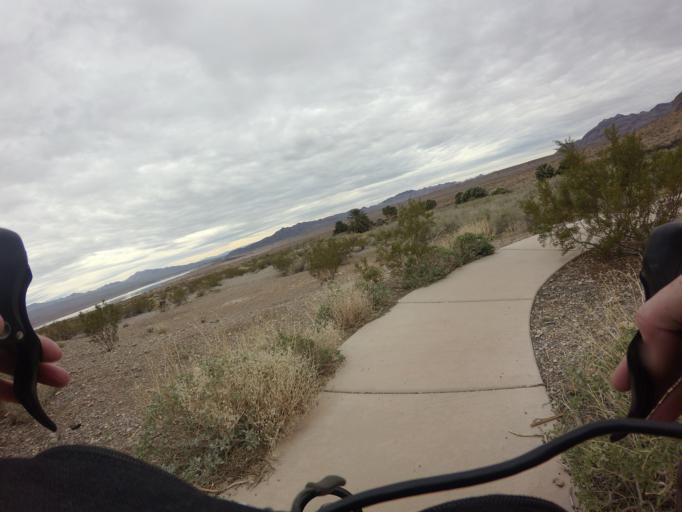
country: US
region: Nevada
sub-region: Clark County
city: Moapa Valley
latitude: 36.3776
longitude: -114.4430
